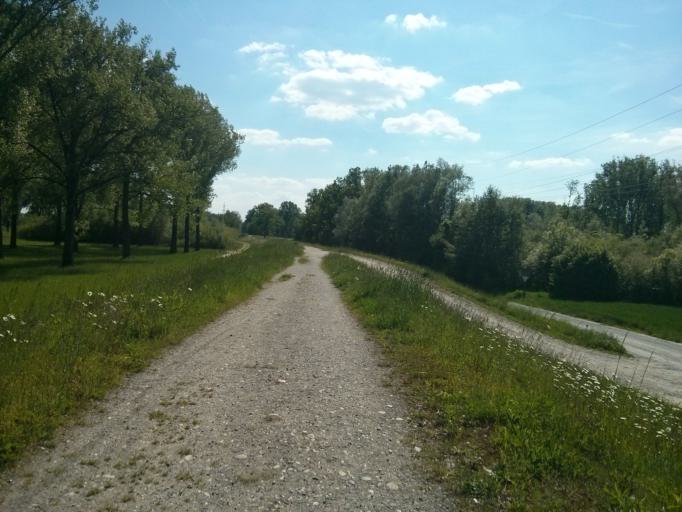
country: DE
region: Bavaria
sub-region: Lower Bavaria
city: Plattling
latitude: 48.7666
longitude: 12.8718
